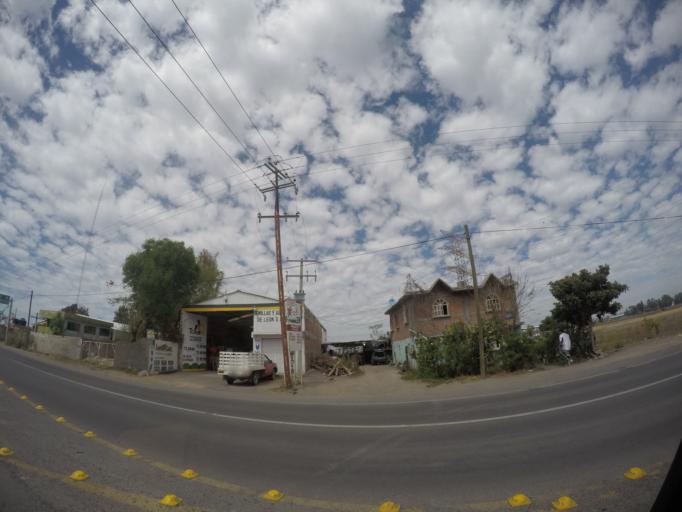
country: MX
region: Guanajuato
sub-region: Leon
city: El CERESO
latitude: 21.0261
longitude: -101.6968
